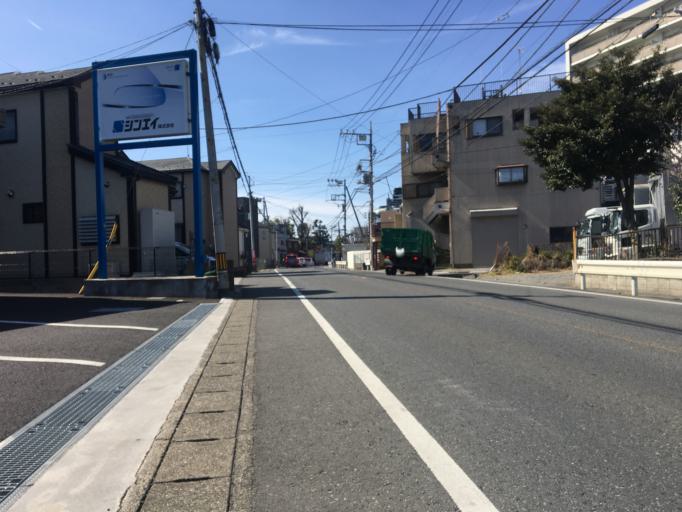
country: JP
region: Saitama
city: Asaka
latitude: 35.7992
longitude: 139.5750
